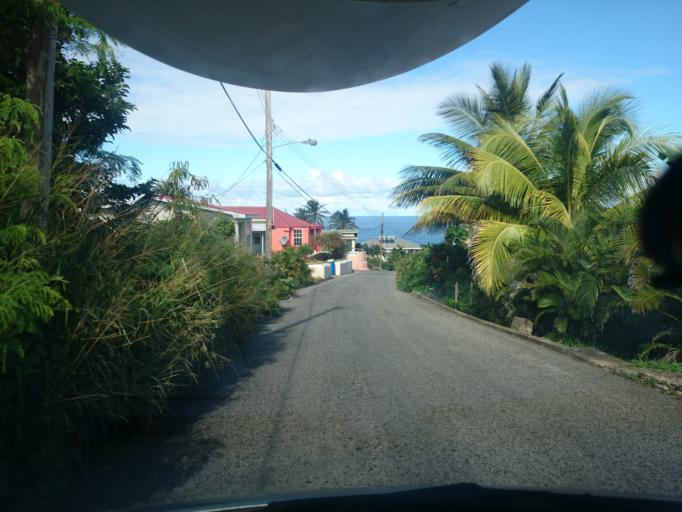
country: BB
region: Saint Joseph
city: Bathsheba
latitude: 13.2132
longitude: -59.5269
